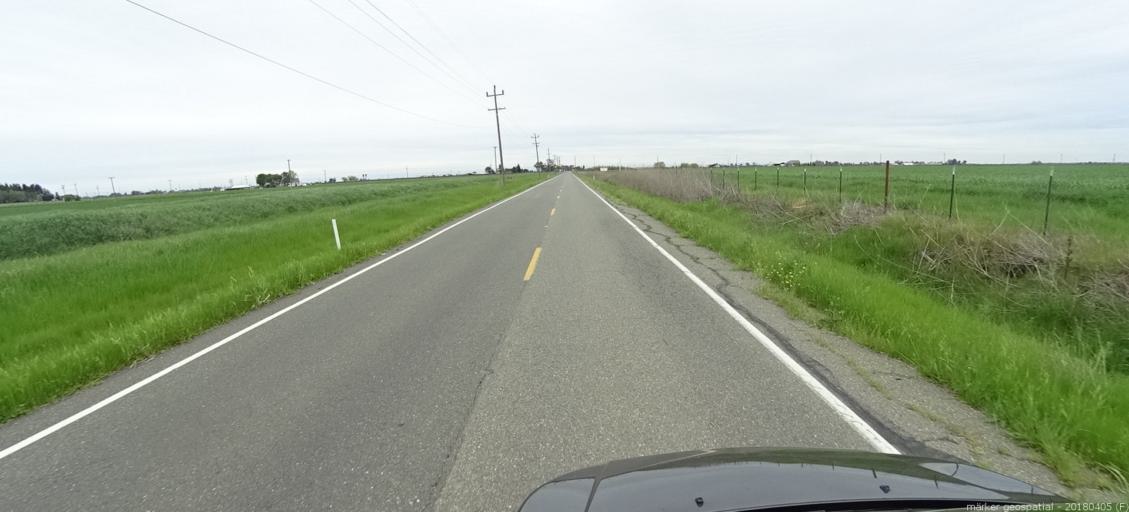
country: US
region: California
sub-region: San Joaquin County
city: Thornton
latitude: 38.3208
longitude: -121.4511
